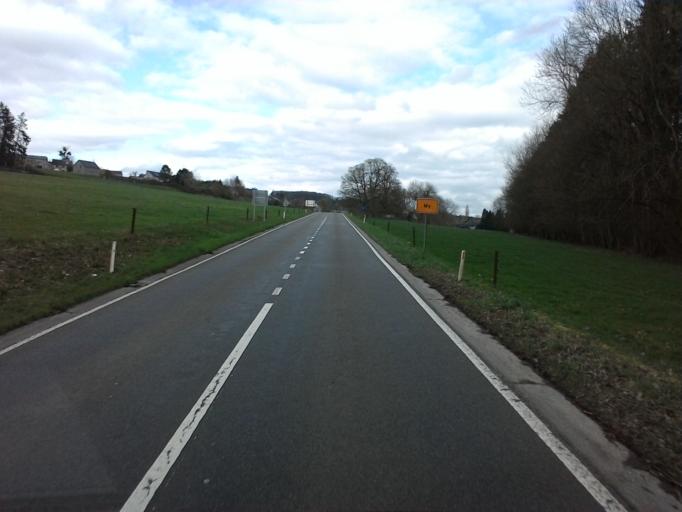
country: BE
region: Wallonia
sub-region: Province de Liege
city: Hamoir
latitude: 50.4028
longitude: 5.5663
